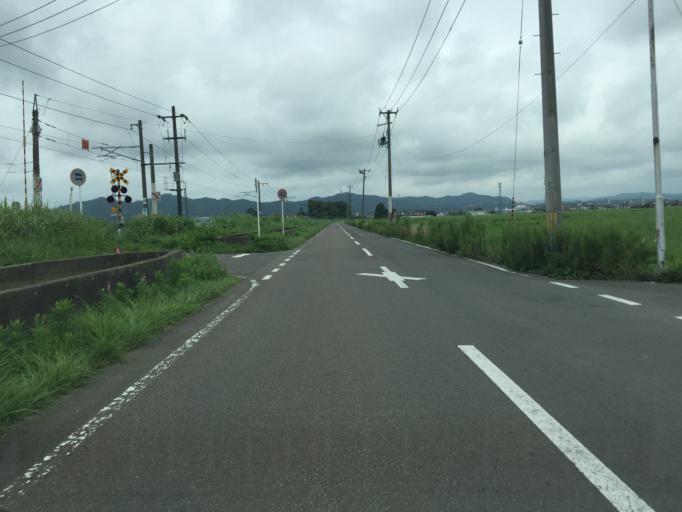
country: JP
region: Miyagi
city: Watari
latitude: 38.0276
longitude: 140.8729
